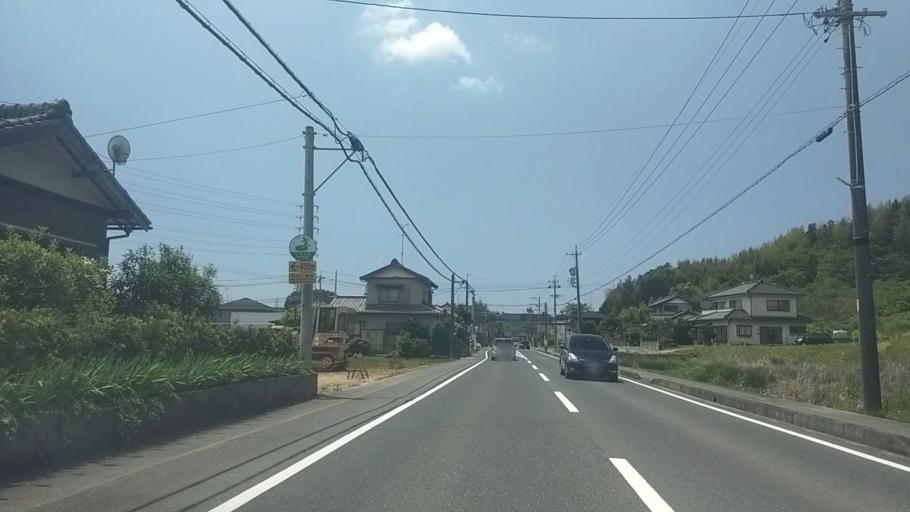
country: JP
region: Shizuoka
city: Hamamatsu
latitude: 34.7683
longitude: 137.6639
